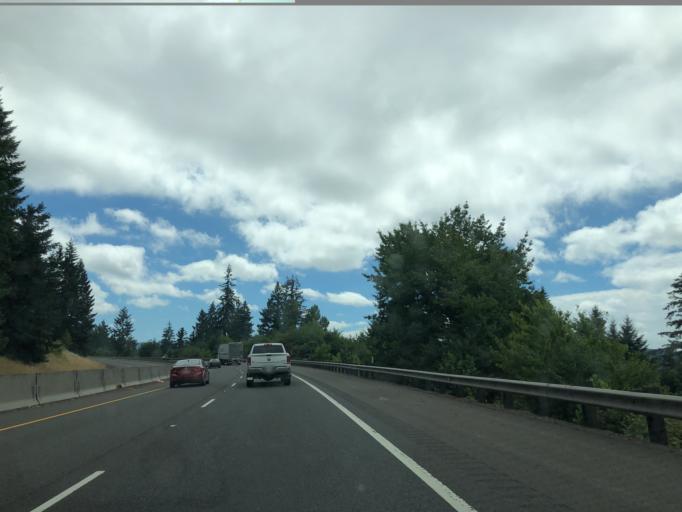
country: US
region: Oregon
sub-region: Lane County
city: Cottage Grove
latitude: 43.7919
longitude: -123.0520
